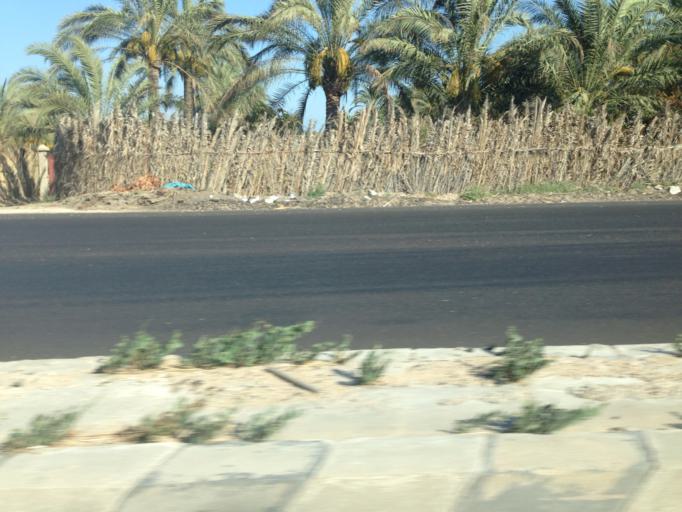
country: EG
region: Al Buhayrah
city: Idku
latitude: 31.3007
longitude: 30.2674
